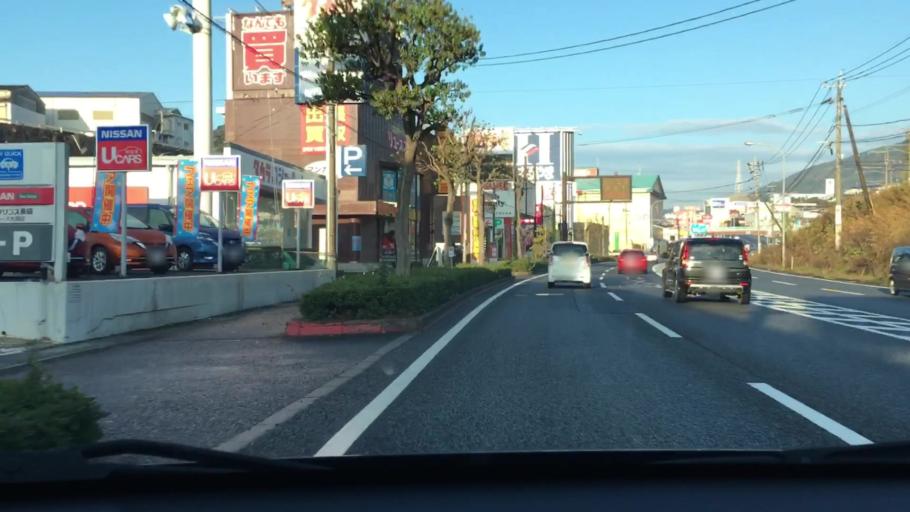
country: JP
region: Nagasaki
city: Sasebo
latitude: 33.1532
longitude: 129.7747
